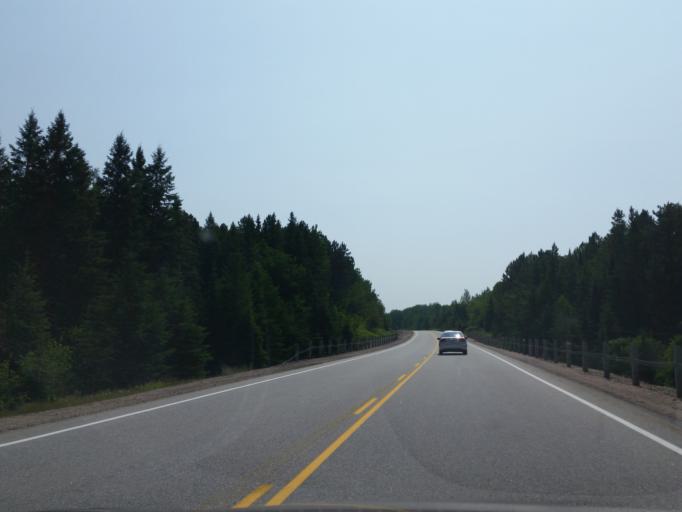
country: CA
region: Ontario
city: Mattawa
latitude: 46.2790
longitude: -78.4906
